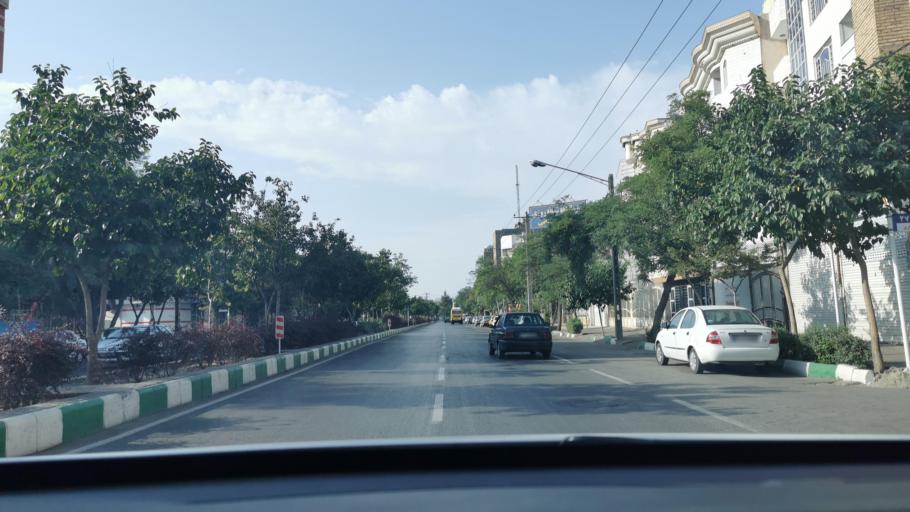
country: IR
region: Razavi Khorasan
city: Mashhad
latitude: 36.2671
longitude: 59.6195
